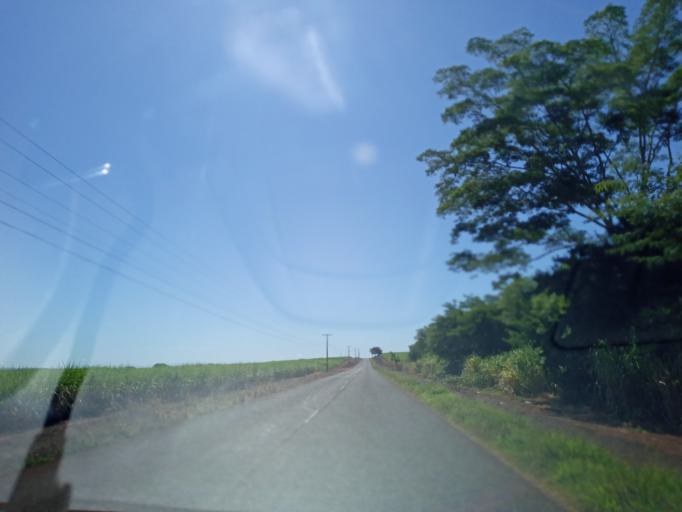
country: BR
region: Goias
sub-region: Itumbiara
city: Itumbiara
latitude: -18.4255
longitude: -49.1731
